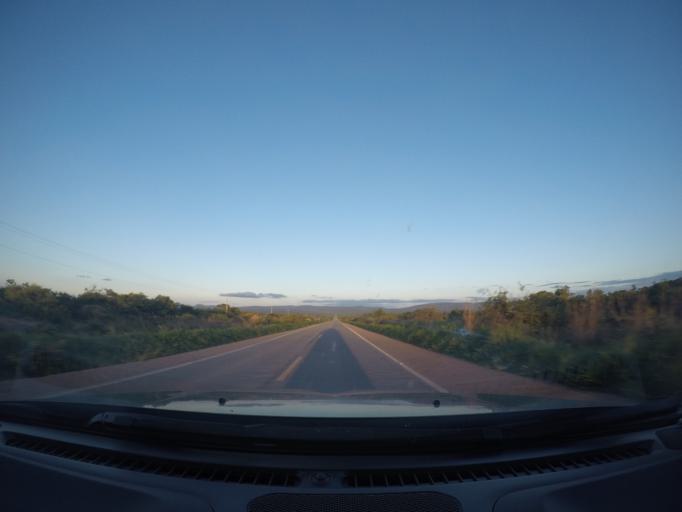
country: BR
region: Bahia
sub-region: Seabra
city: Seabra
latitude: -12.4078
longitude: -41.9629
